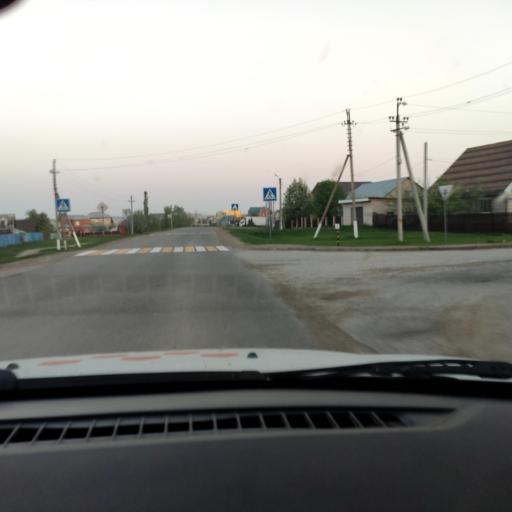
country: RU
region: Bashkortostan
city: Karmaskaly
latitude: 54.3656
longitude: 56.1578
